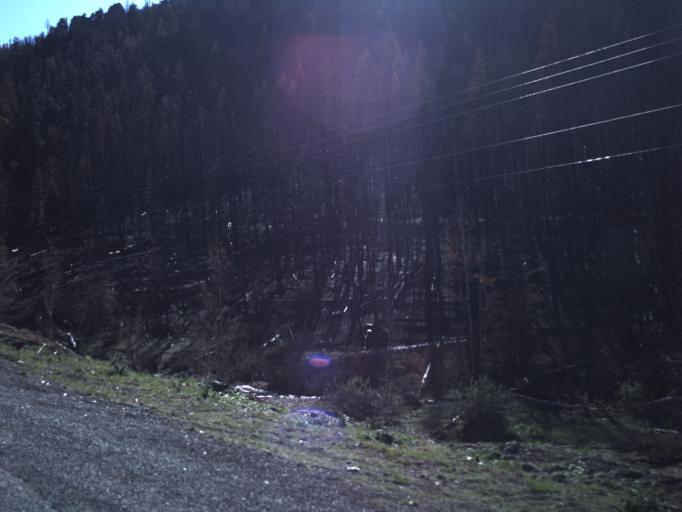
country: US
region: Utah
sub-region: Iron County
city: Parowan
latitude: 37.7402
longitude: -112.8380
